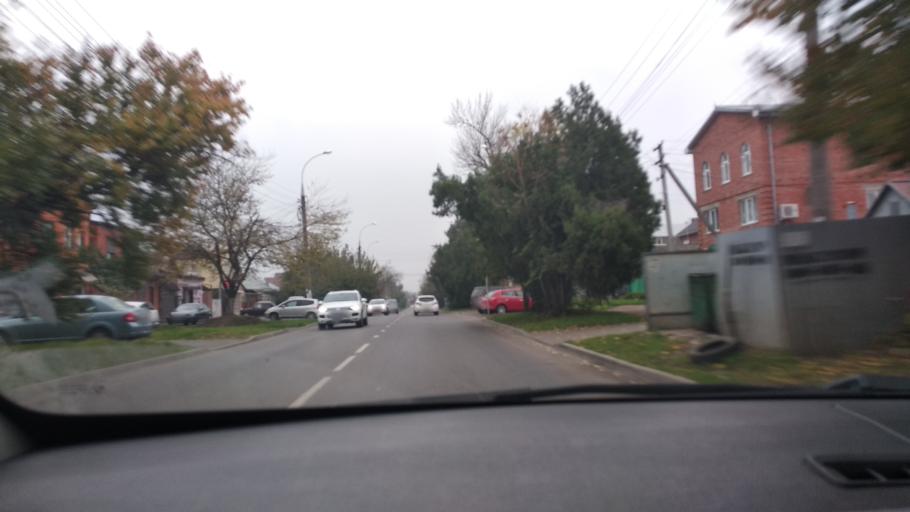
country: RU
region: Krasnodarskiy
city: Krasnodar
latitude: 45.0191
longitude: 39.0102
